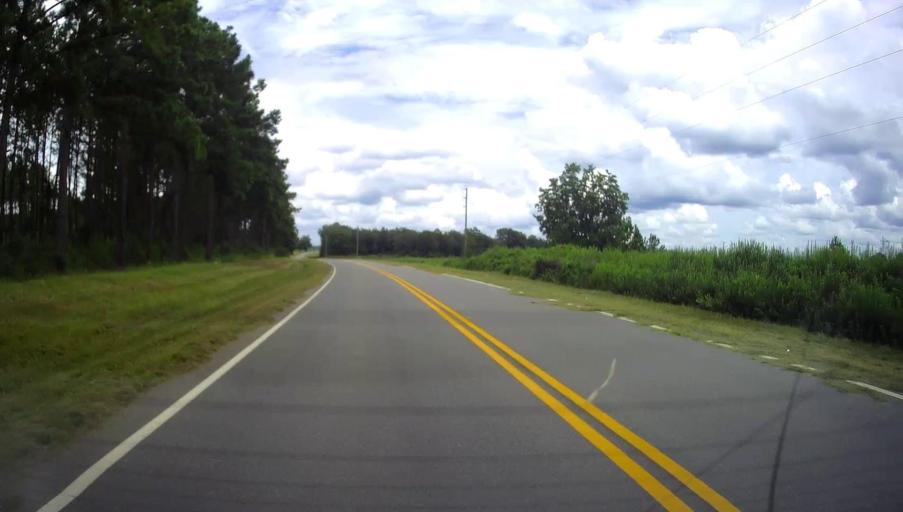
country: US
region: Georgia
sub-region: Schley County
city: Ellaville
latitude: 32.2678
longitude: -84.1863
